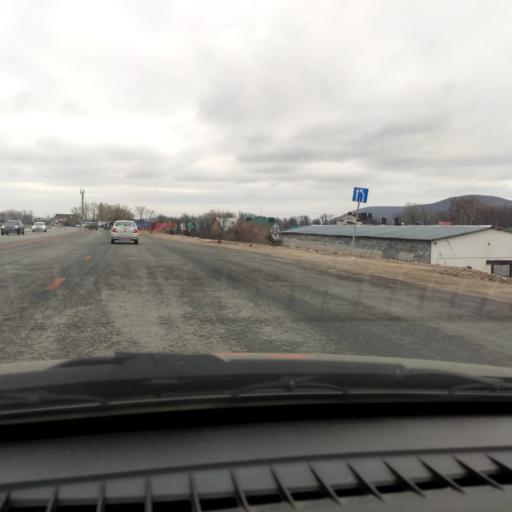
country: RU
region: Samara
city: Volzhskiy
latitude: 53.4195
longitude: 50.1274
